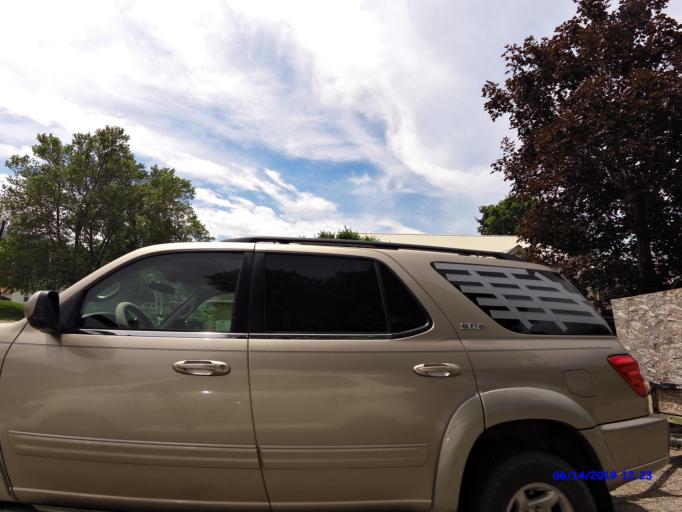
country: US
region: Utah
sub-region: Weber County
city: Ogden
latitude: 41.2557
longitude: -111.9487
